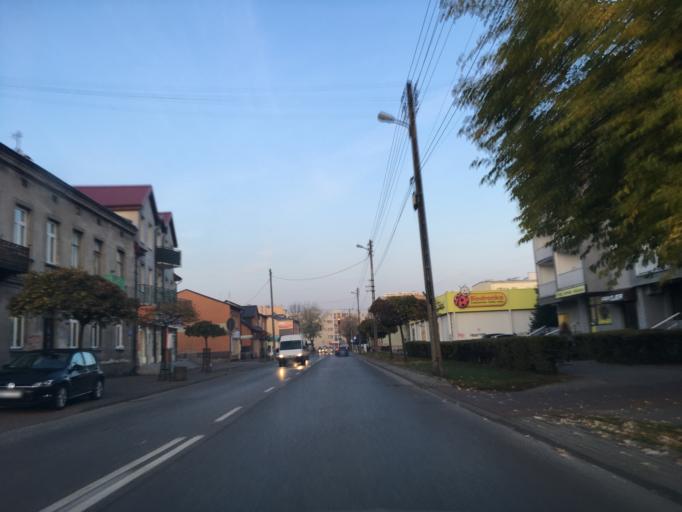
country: PL
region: Lodz Voivodeship
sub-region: Skierniewice
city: Skierniewice
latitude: 51.9562
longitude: 20.1483
